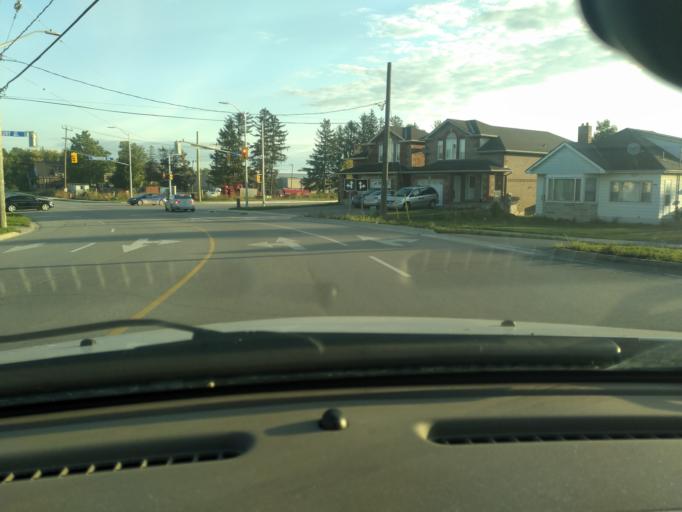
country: CA
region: Ontario
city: Bradford West Gwillimbury
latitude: 44.1093
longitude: -79.5636
